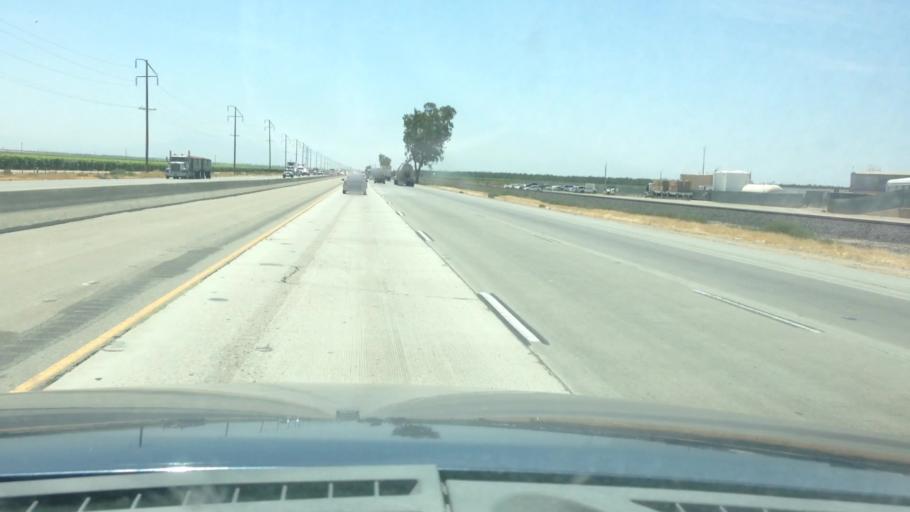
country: US
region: California
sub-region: Kern County
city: Rosedale
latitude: 35.4851
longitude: -119.1454
